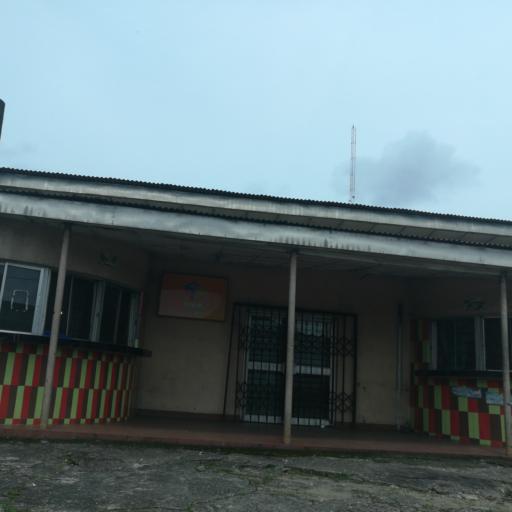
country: NG
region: Rivers
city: Port Harcourt
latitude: 4.7991
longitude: 7.0048
